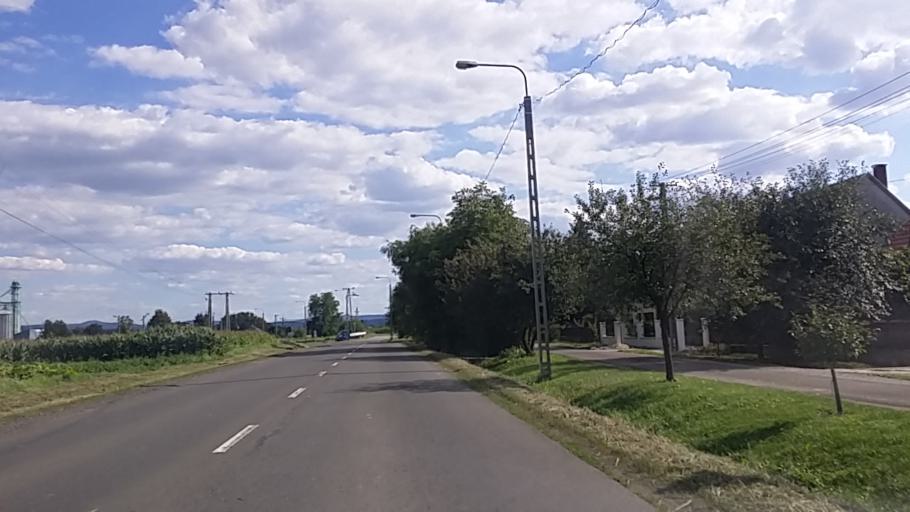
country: HU
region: Baranya
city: Sasd
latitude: 46.2659
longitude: 18.1045
